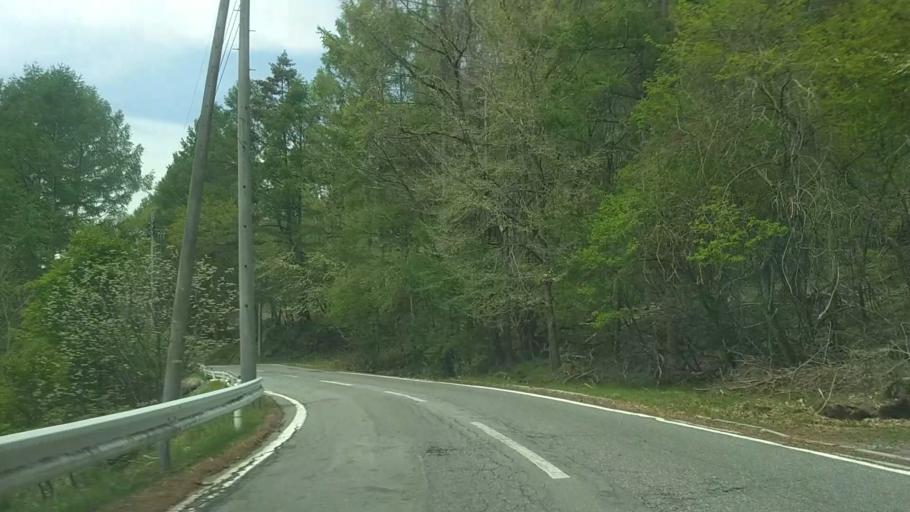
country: JP
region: Nagano
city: Chino
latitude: 36.0429
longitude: 138.2769
